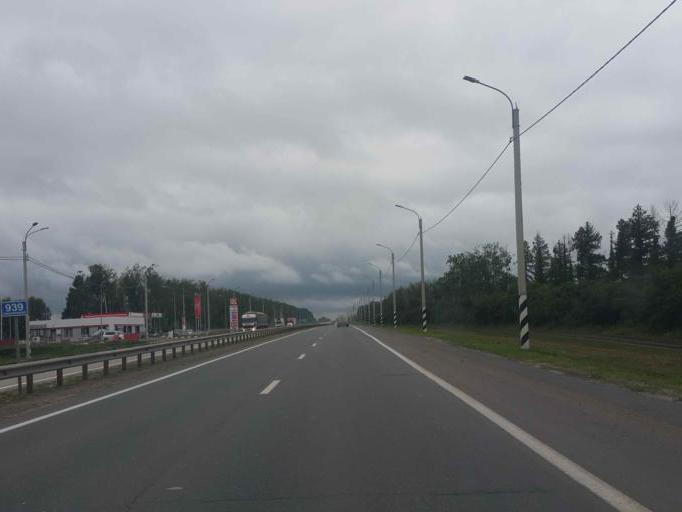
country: RU
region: Tambov
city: Komsomolets
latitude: 52.7353
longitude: 41.2767
